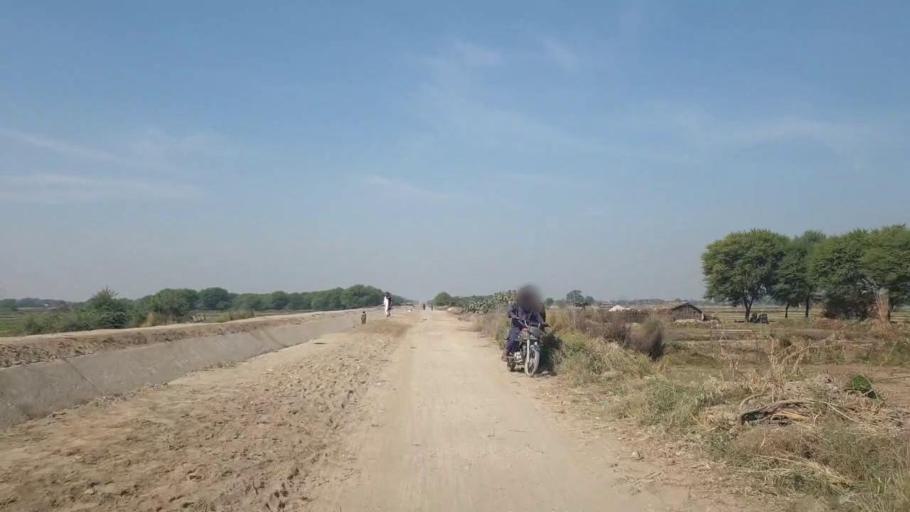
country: PK
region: Sindh
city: Matiari
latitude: 25.6780
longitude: 68.3441
